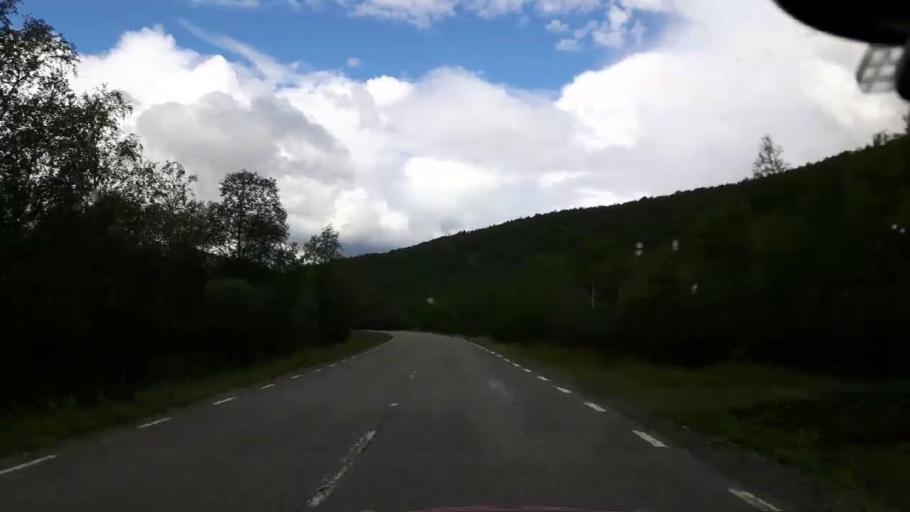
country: NO
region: Nordland
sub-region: Hattfjelldal
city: Hattfjelldal
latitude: 65.0664
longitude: 14.6869
